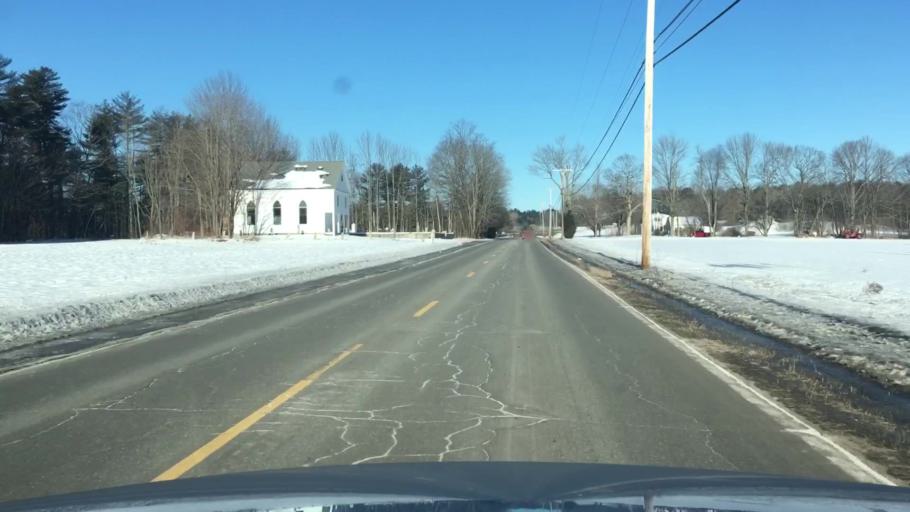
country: US
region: Maine
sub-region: Androscoggin County
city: Lewiston
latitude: 44.0524
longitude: -70.2013
